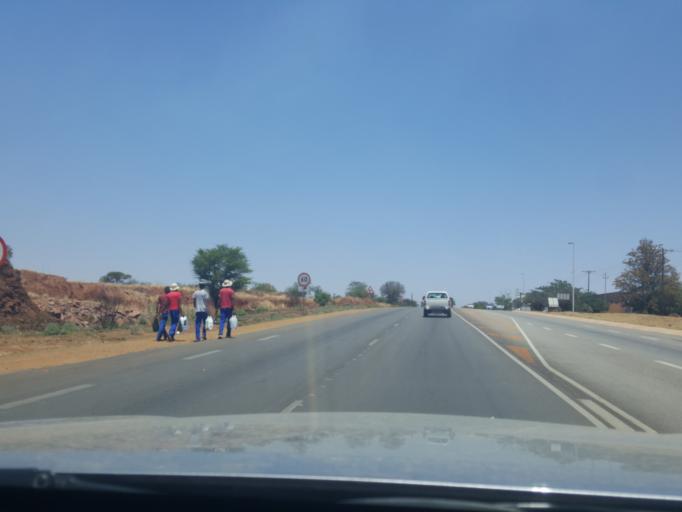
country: ZA
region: North-West
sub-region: Ngaka Modiri Molema District Municipality
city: Zeerust
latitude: -25.5507
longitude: 26.0725
